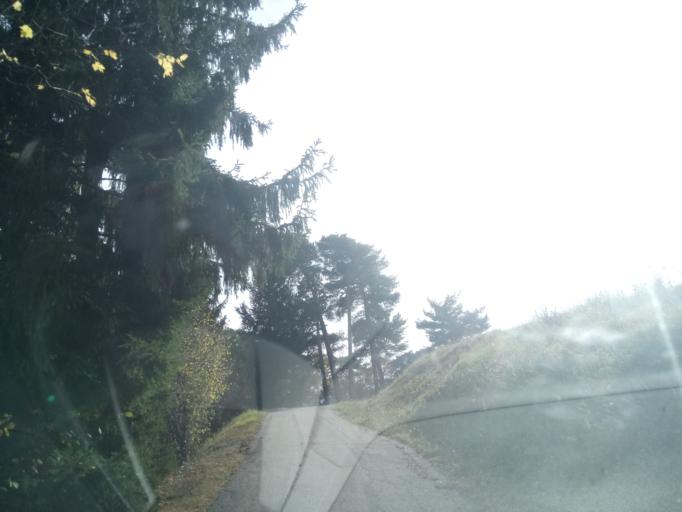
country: FR
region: Rhone-Alpes
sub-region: Departement de la Savoie
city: La Chambre
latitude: 45.3853
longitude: 6.3070
